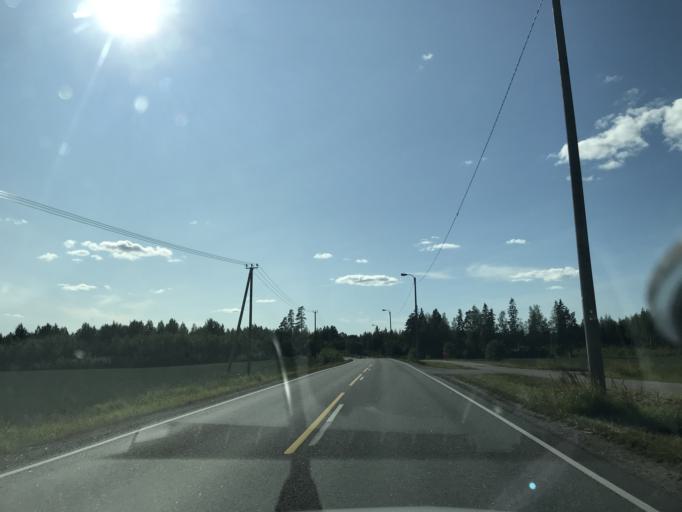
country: FI
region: Uusimaa
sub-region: Helsinki
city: Nurmijaervi
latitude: 60.3850
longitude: 24.7130
